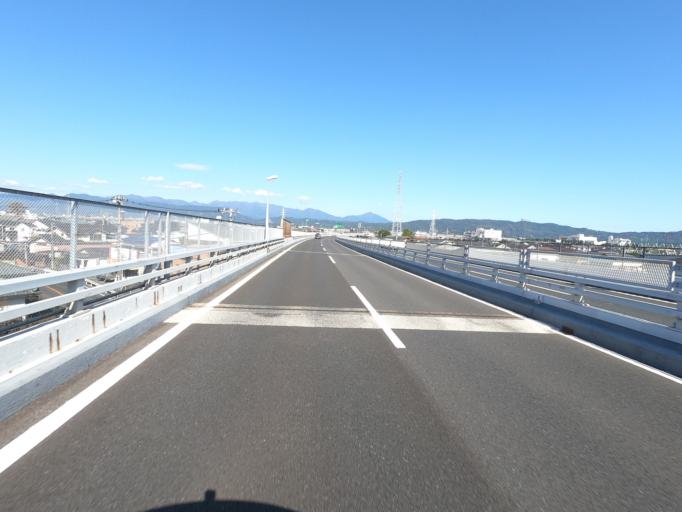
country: JP
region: Kanagawa
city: Odawara
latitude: 35.2781
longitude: 139.1513
